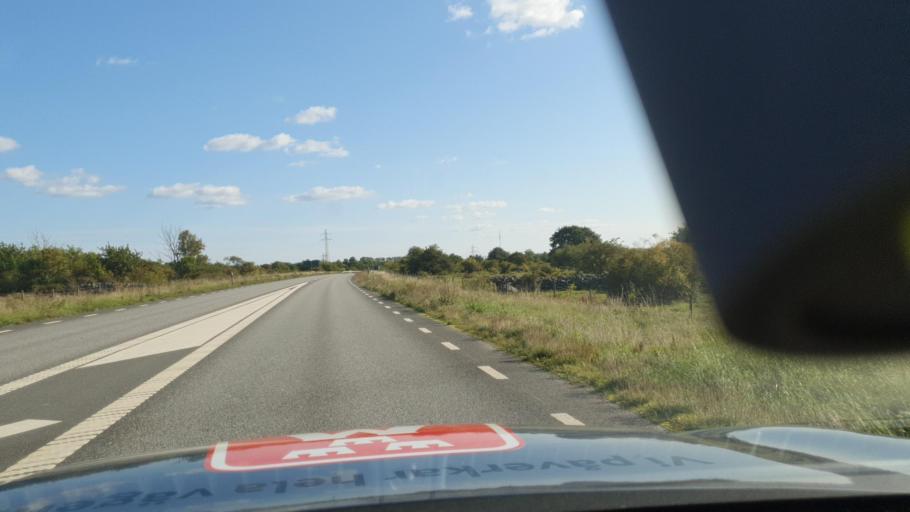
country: SE
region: Skane
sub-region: Bromolla Kommun
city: Bromoella
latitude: 56.0833
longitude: 14.4969
